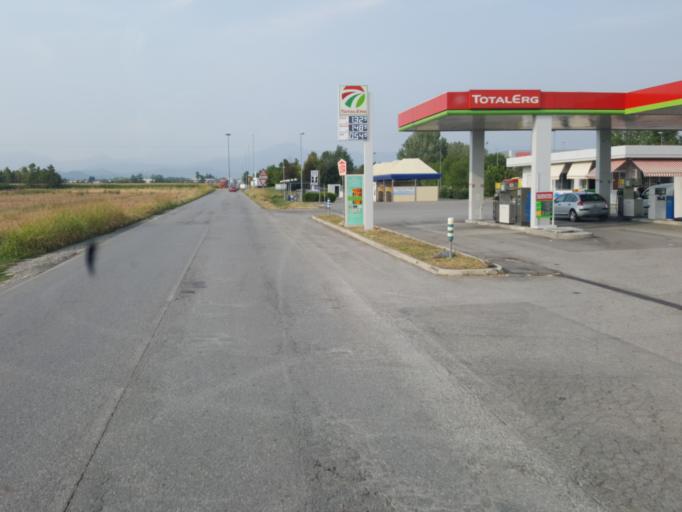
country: IT
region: Lombardy
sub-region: Provincia di Bergamo
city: Mornico al Serio
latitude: 45.6055
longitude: 9.8073
